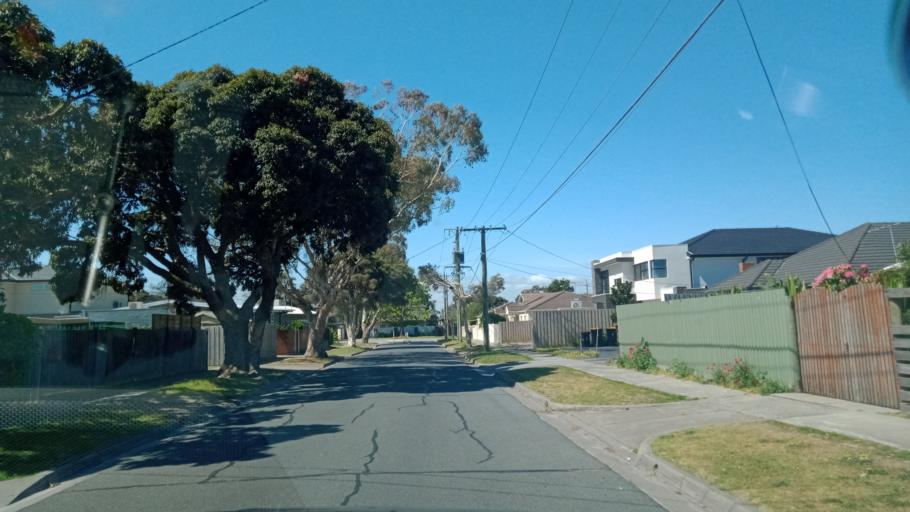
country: AU
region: Victoria
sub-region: Kingston
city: Bonbeach
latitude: -38.0551
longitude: 145.1279
